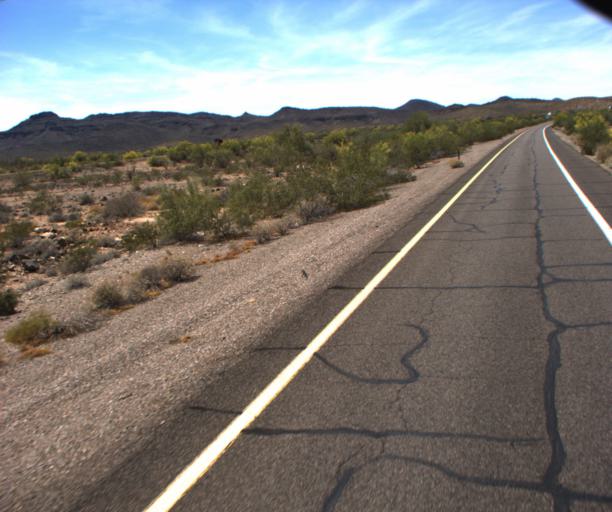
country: US
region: Arizona
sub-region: La Paz County
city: Quartzsite
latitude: 33.6636
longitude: -114.0109
